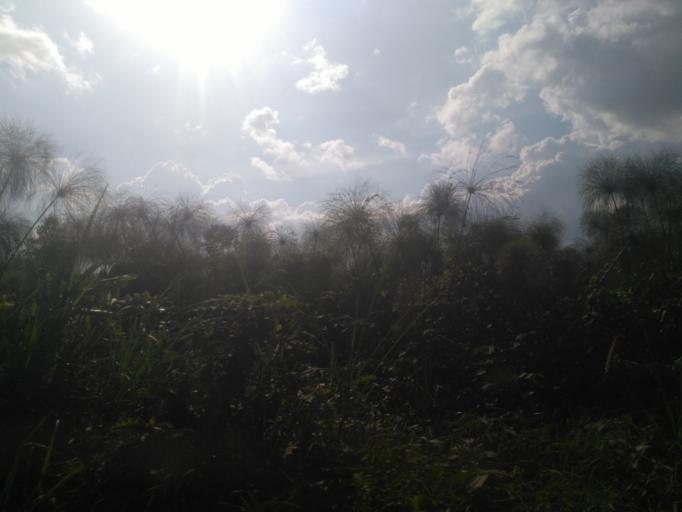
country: UG
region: Central Region
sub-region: Wakiso District
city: Wakiso
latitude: 0.3090
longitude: 32.4435
